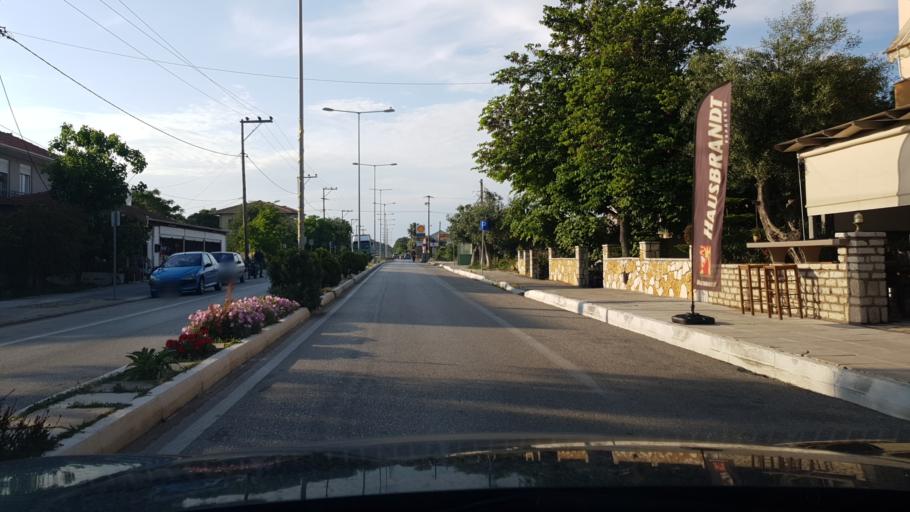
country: GR
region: Ionian Islands
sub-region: Lefkada
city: Lefkada
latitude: 38.7917
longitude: 20.7185
